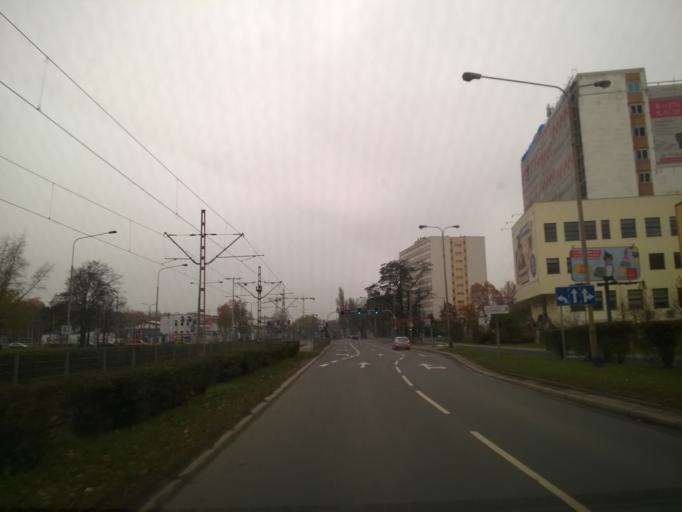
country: PL
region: Lower Silesian Voivodeship
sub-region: Powiat wroclawski
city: Wroclaw
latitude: 51.0903
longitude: 17.0288
